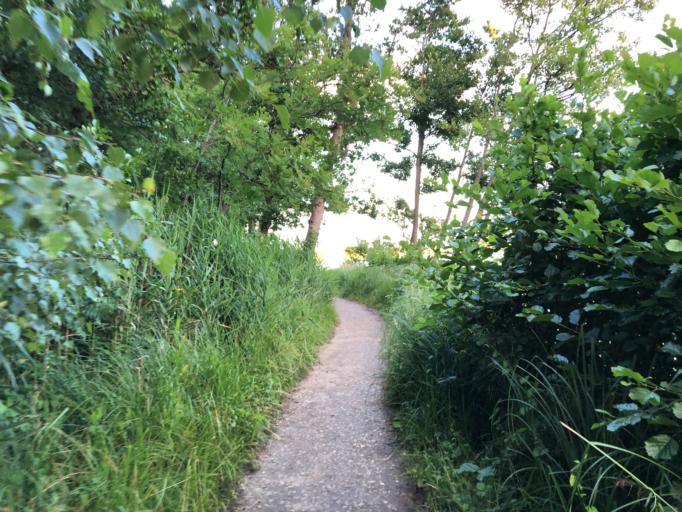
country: DK
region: Capital Region
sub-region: Gladsaxe Municipality
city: Buddinge
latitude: 55.7767
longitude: 12.4755
